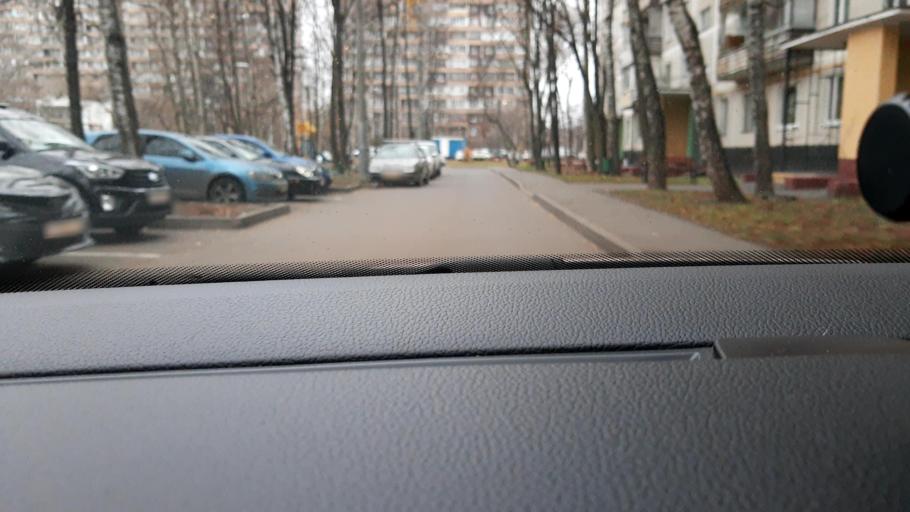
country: RU
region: Moscow
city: Gol'yanovo
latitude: 55.8279
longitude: 37.8236
